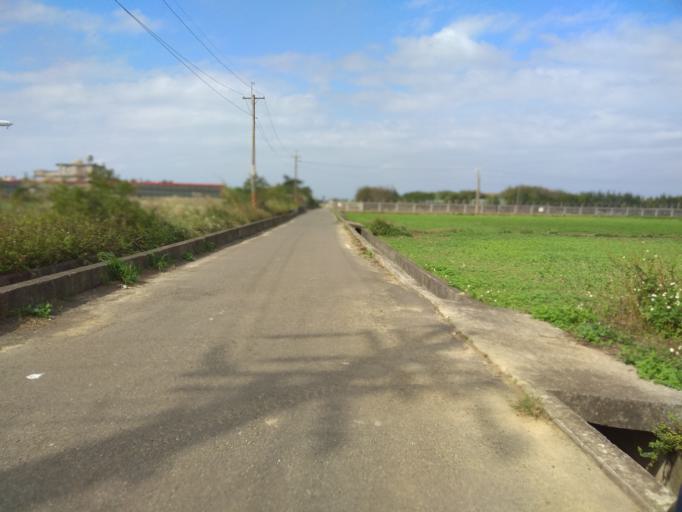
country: TW
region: Taiwan
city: Taoyuan City
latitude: 25.0642
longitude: 121.2137
